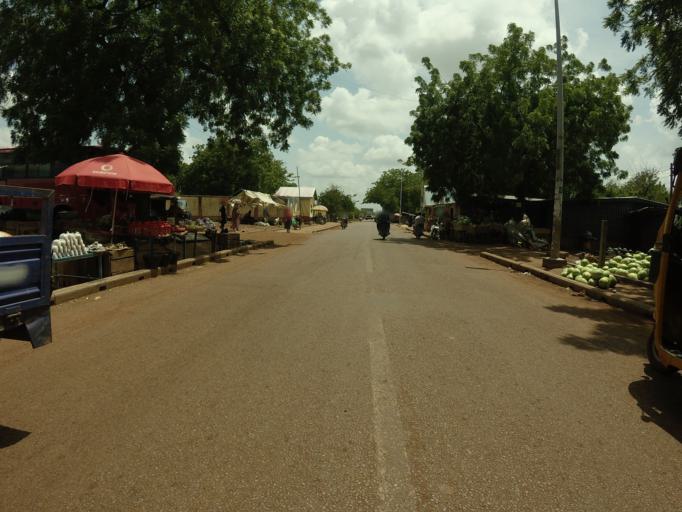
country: GH
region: Northern
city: Tamale
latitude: 9.4014
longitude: -0.8486
